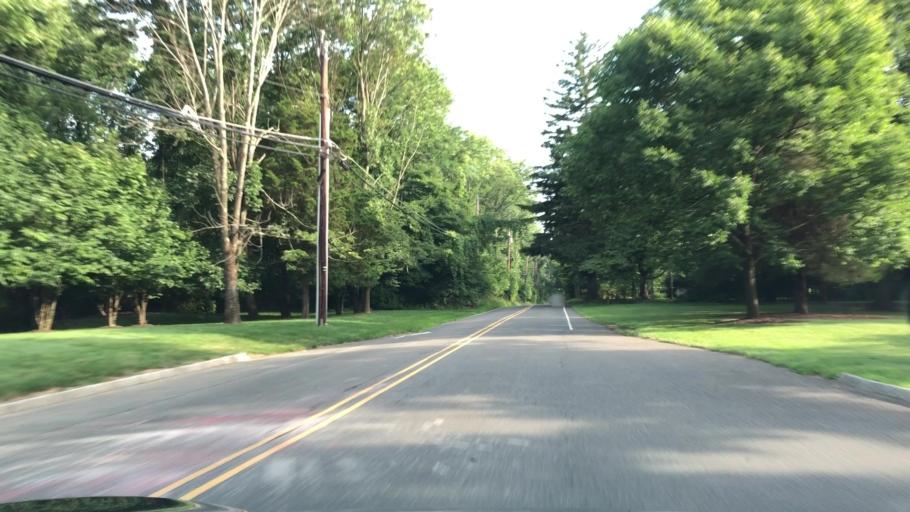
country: US
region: New Jersey
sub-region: Mercer County
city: Lawrenceville
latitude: 40.3290
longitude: -74.7023
